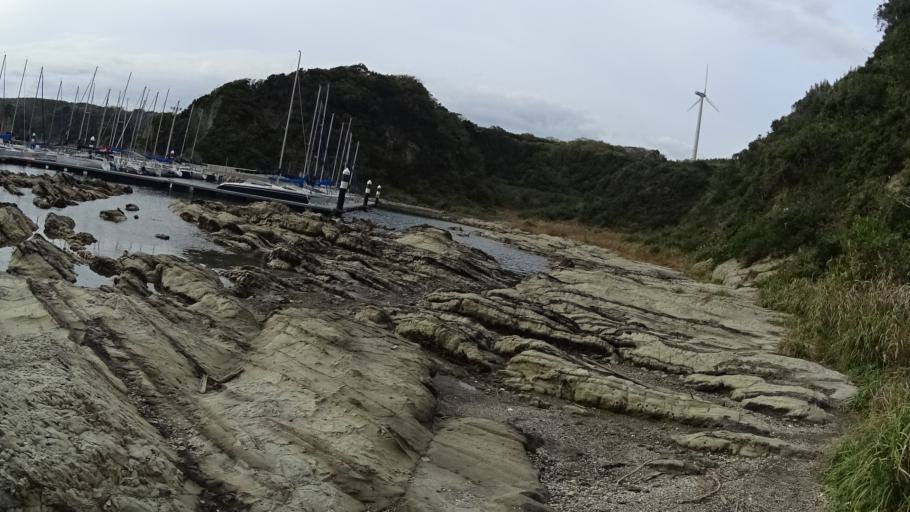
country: JP
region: Kanagawa
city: Miura
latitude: 35.1404
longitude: 139.6406
